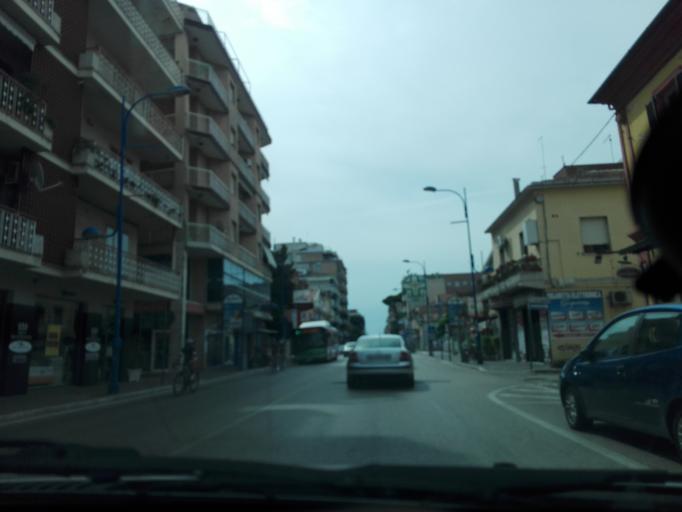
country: IT
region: Abruzzo
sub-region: Provincia di Pescara
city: Montesilvano Marina
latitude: 42.5154
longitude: 14.1513
